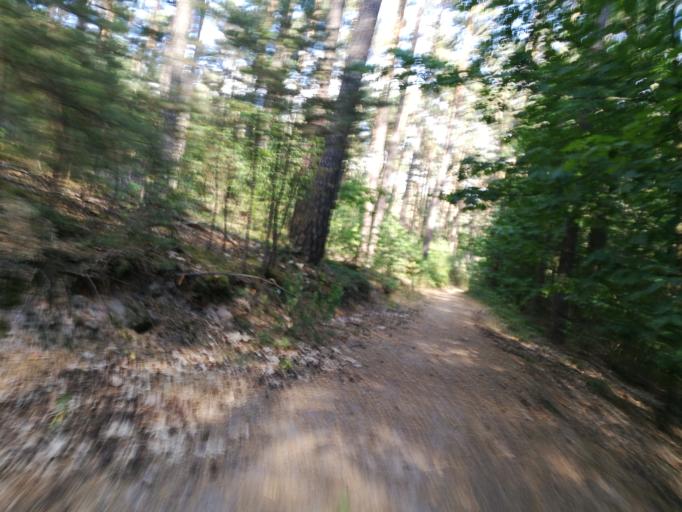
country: DE
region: Bavaria
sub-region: Regierungsbezirk Mittelfranken
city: Seukendorf
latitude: 49.4726
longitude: 10.9237
